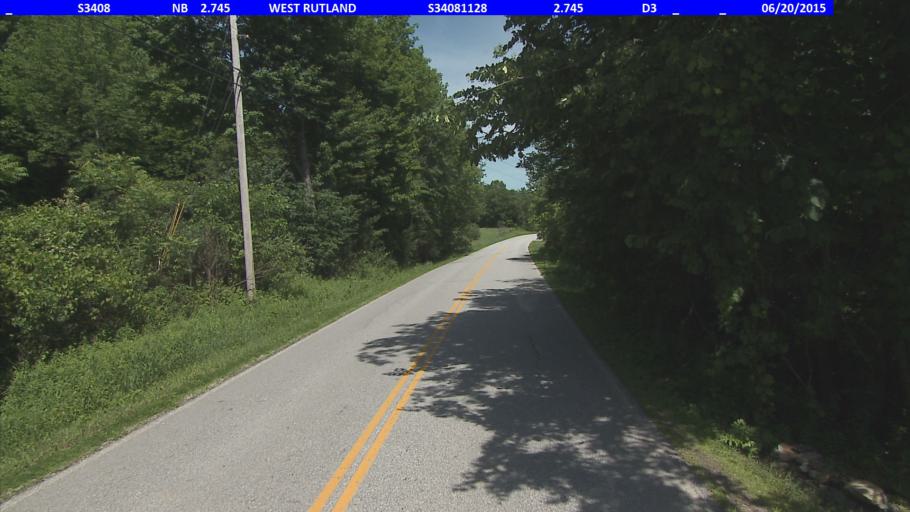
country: US
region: Vermont
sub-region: Rutland County
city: West Rutland
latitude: 43.6484
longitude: -73.0725
